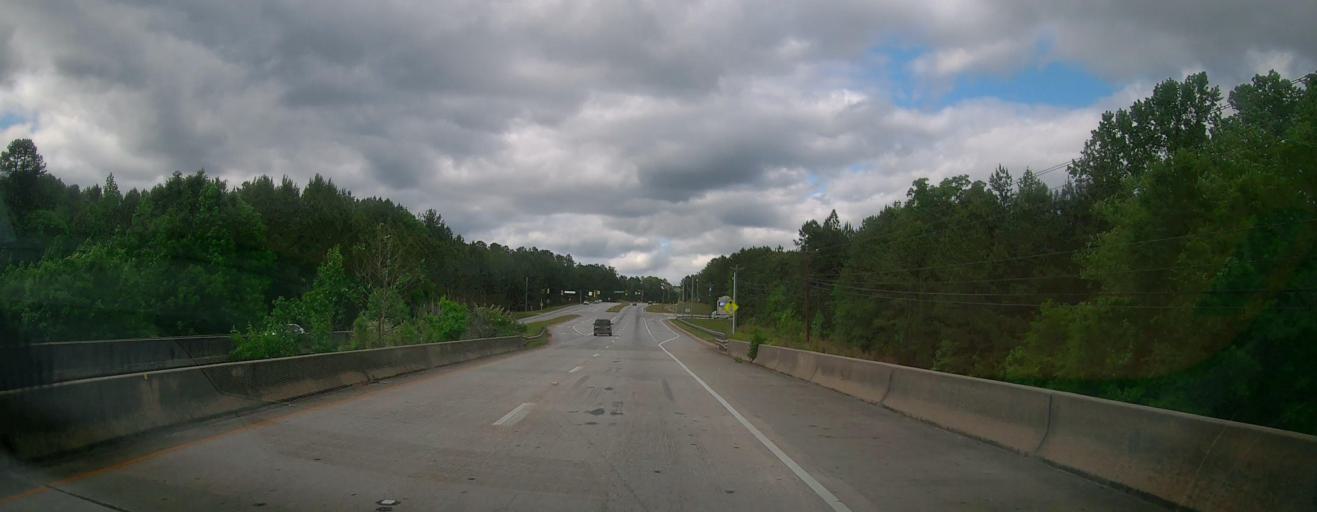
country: US
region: Georgia
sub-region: Rockdale County
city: Conyers
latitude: 33.6870
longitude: -83.9621
